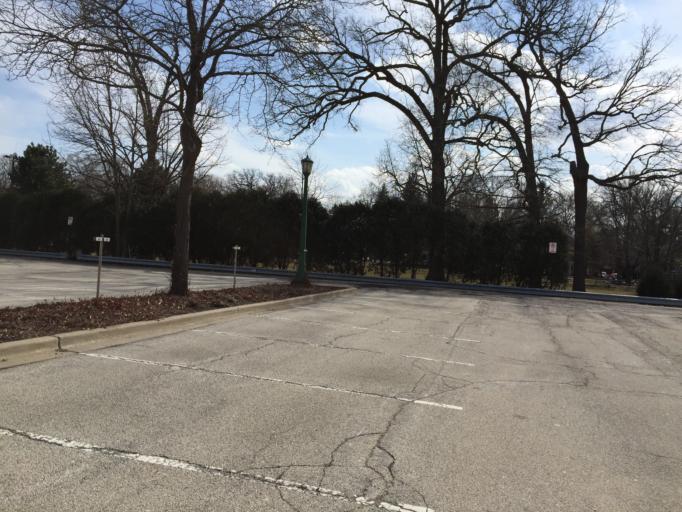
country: US
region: Illinois
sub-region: Cook County
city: Kenilworth
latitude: 42.0723
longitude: -87.6912
